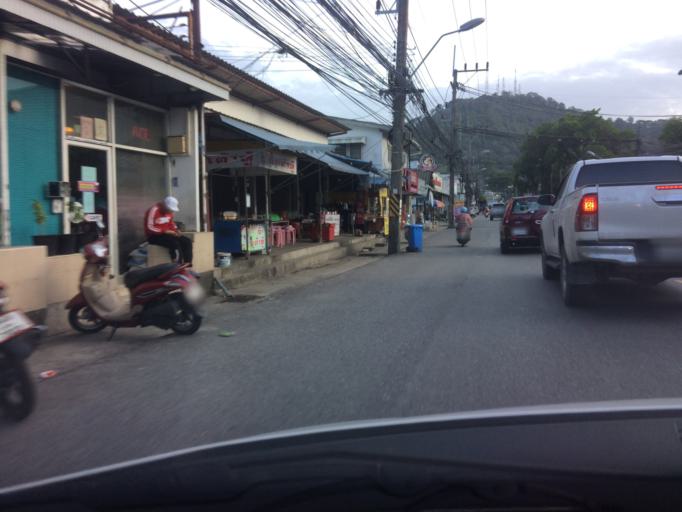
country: TH
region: Phuket
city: Ban Talat Yai
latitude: 7.8845
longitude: 98.3994
